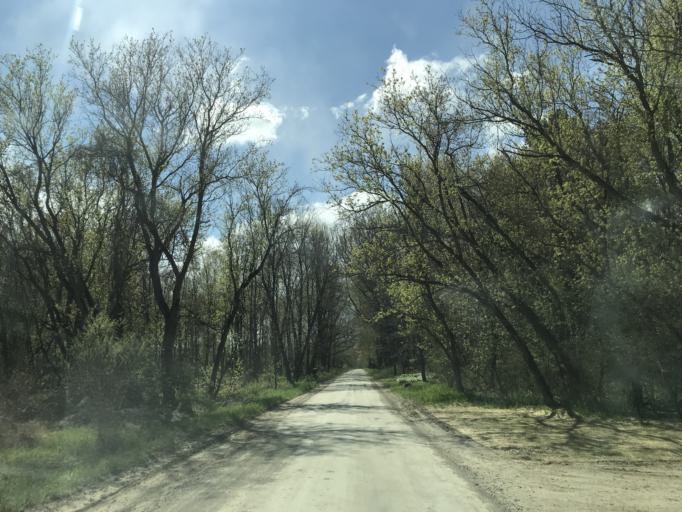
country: US
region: Michigan
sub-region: Oakland County
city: South Lyon
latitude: 42.4037
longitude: -83.6771
